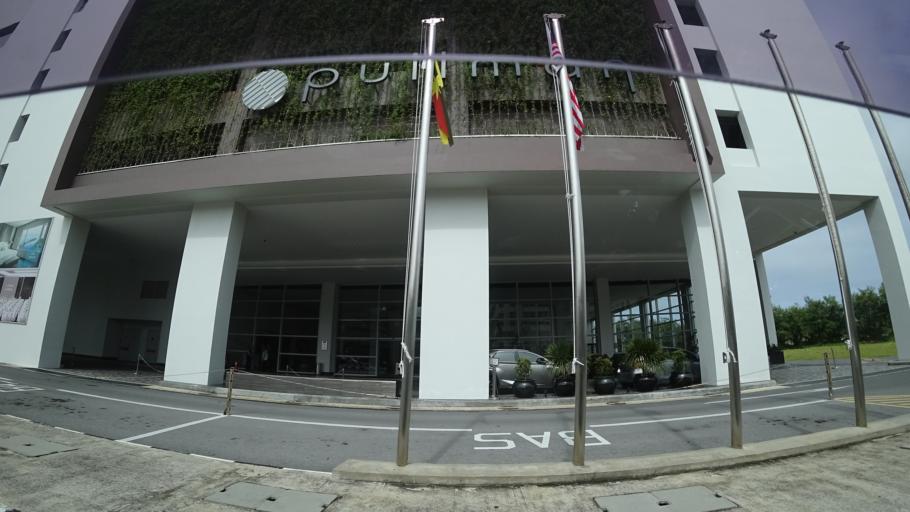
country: MY
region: Sarawak
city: Miri
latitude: 4.3983
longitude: 113.9855
